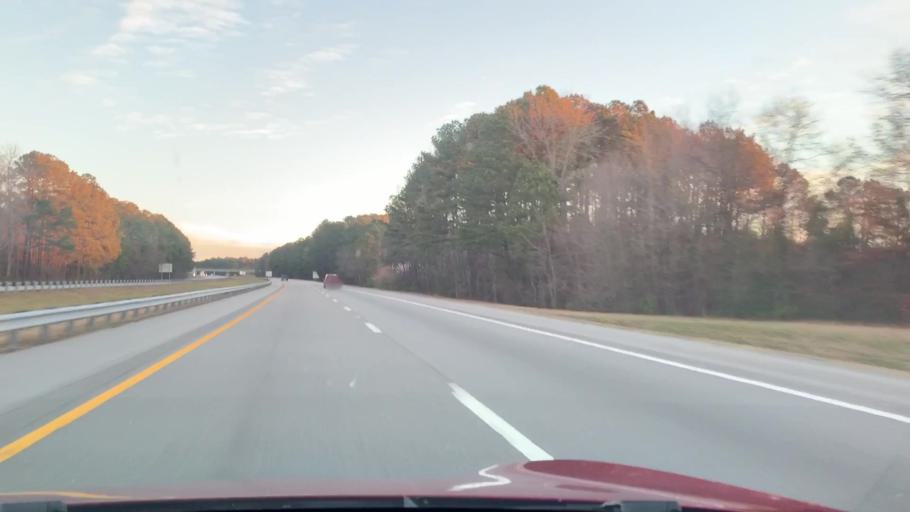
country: US
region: North Carolina
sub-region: Nash County
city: Red Oak
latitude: 36.0768
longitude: -77.8118
